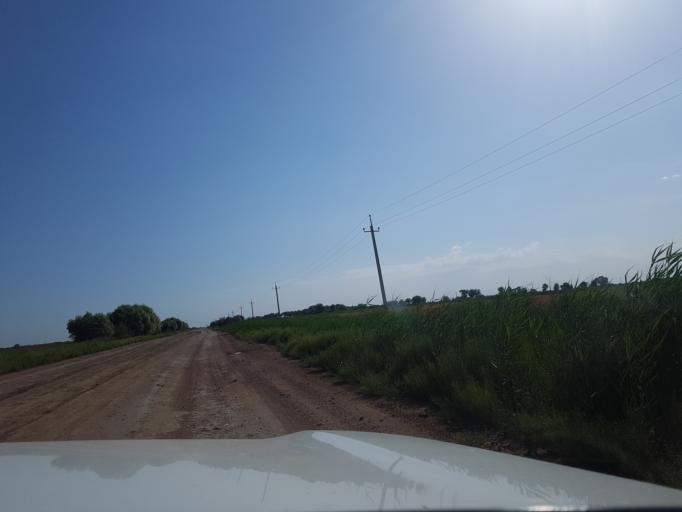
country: TM
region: Dasoguz
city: Koeneuergench
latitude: 42.0423
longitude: 58.8186
